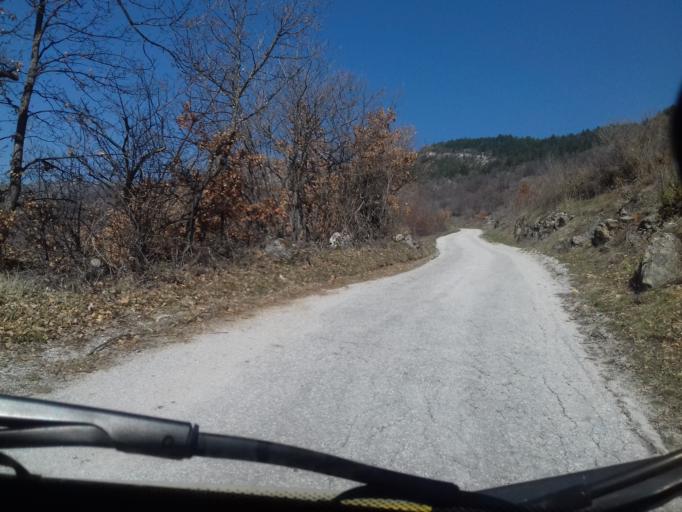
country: BA
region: Federation of Bosnia and Herzegovina
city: Travnik
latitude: 44.2481
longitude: 17.7230
